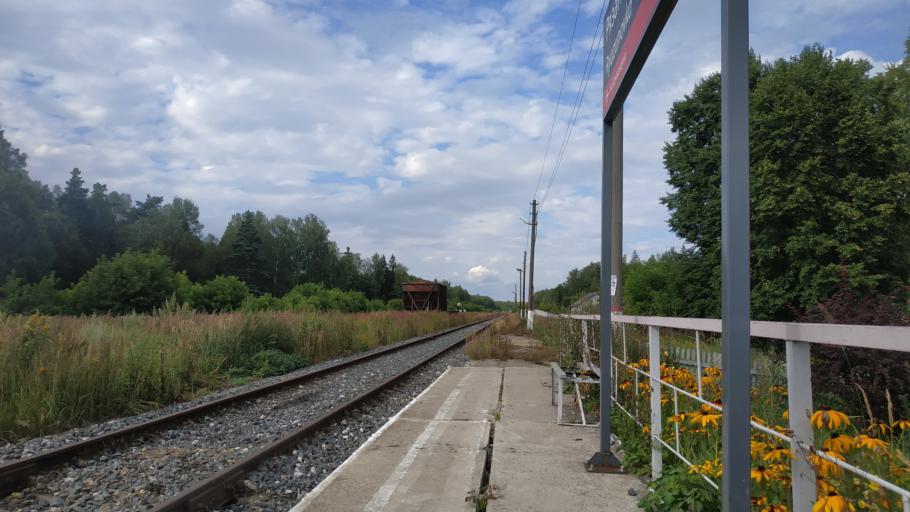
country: RU
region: Moskovskaya
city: Radovitskiy
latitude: 55.1461
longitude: 39.5571
